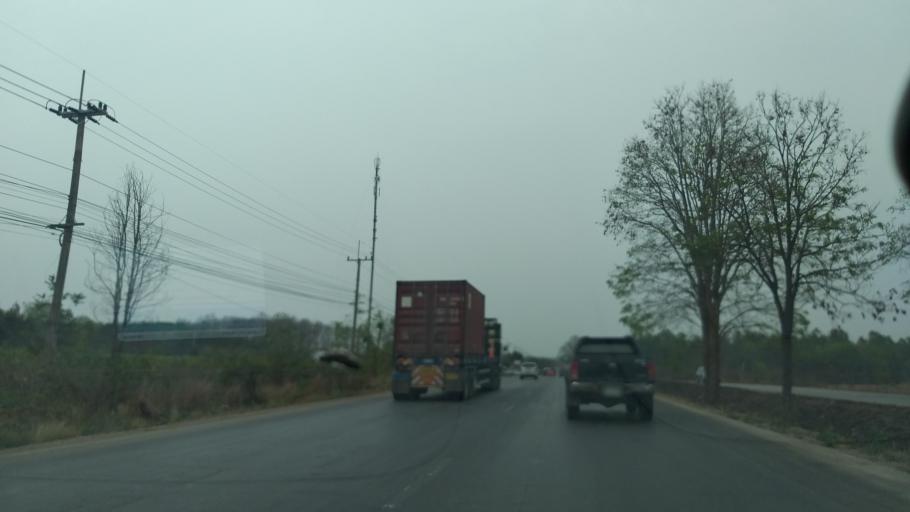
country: TH
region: Chachoengsao
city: Plaeng Yao
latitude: 13.5211
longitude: 101.2656
